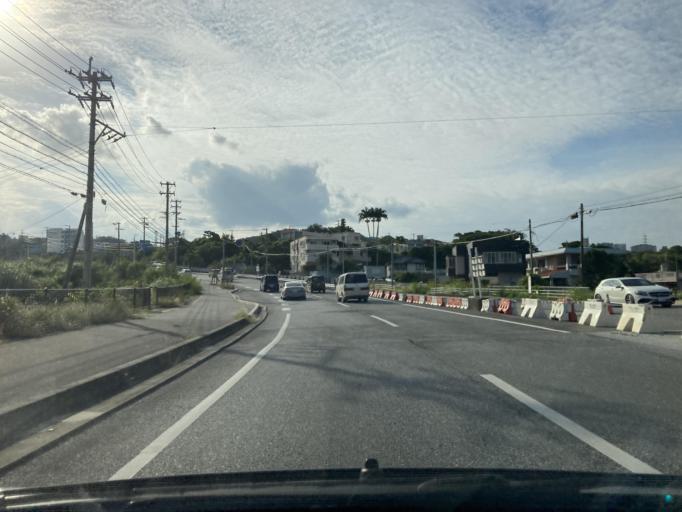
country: JP
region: Okinawa
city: Okinawa
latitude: 26.3028
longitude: 127.8089
